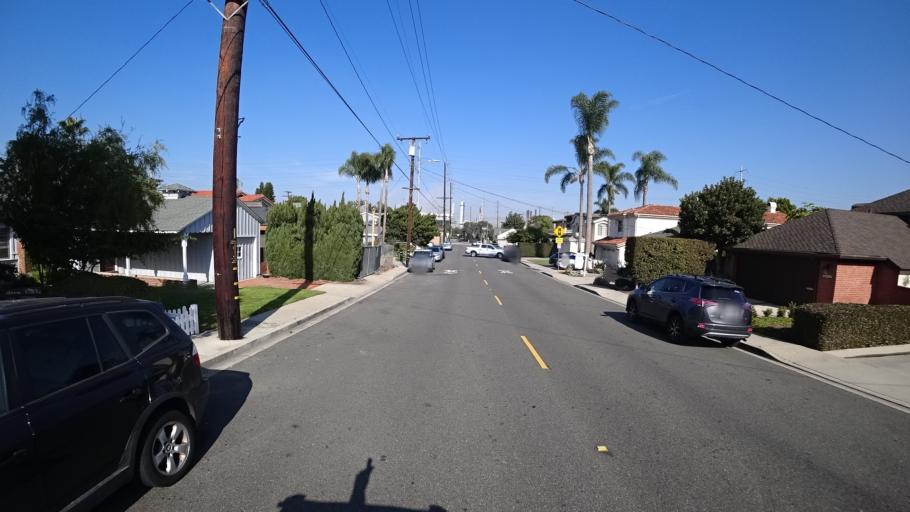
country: US
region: California
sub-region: Los Angeles County
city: Manhattan Beach
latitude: 33.9007
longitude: -118.4035
